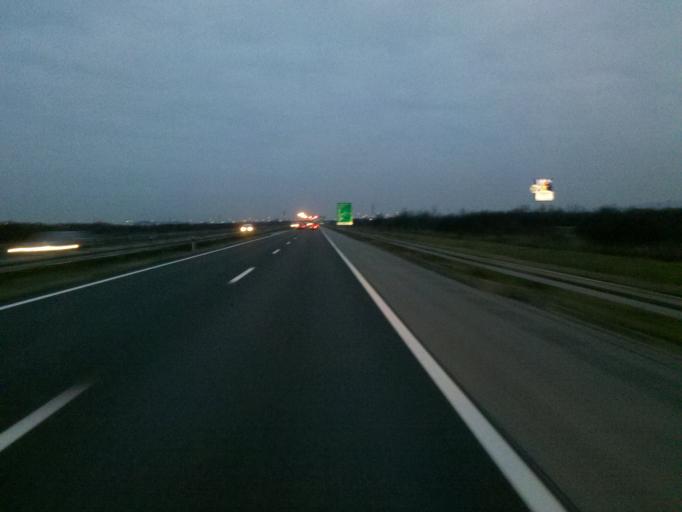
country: HR
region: Grad Zagreb
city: Odra
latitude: 45.7479
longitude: 16.0280
